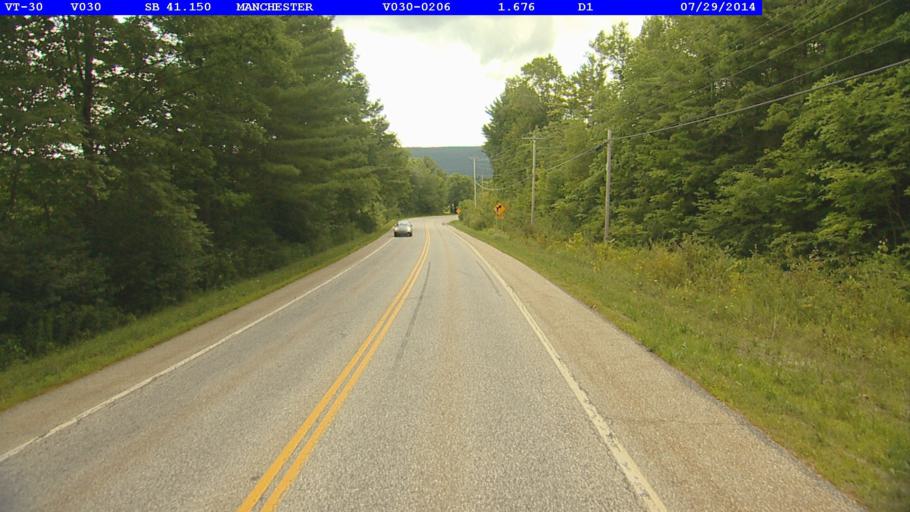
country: US
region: Vermont
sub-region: Bennington County
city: Manchester Center
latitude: 43.1992
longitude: -73.0557
